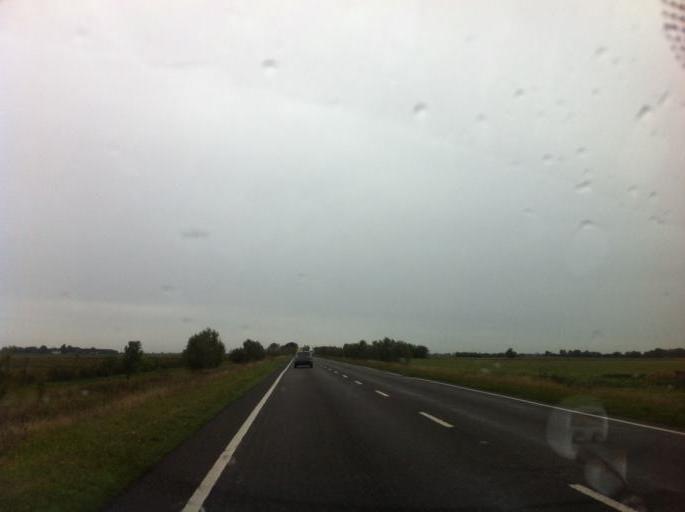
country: GB
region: England
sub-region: Peterborough
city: Eye
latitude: 52.6248
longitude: -0.2052
